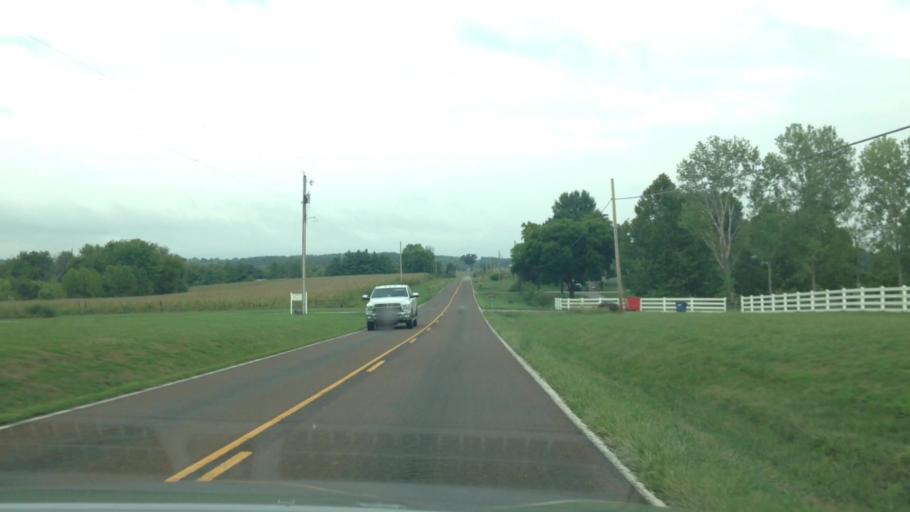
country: US
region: Missouri
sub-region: Clay County
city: Smithville
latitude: 39.4050
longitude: -94.6215
